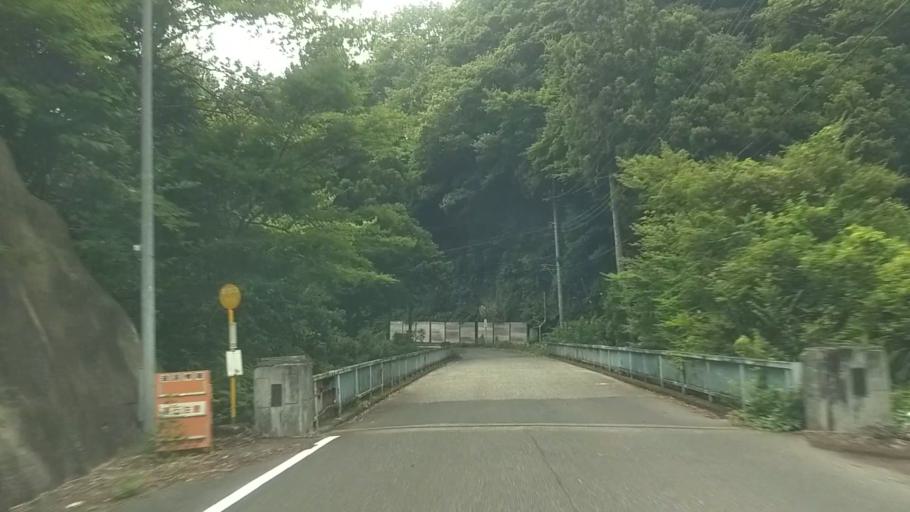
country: JP
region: Chiba
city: Kawaguchi
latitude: 35.1896
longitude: 140.1406
